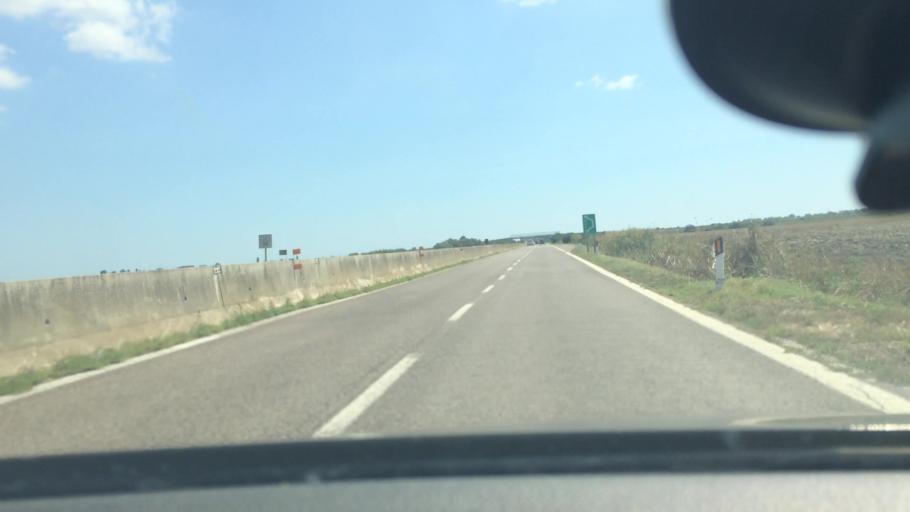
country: IT
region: Emilia-Romagna
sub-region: Provincia di Ferrara
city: Ostellato
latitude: 44.7556
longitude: 11.9740
